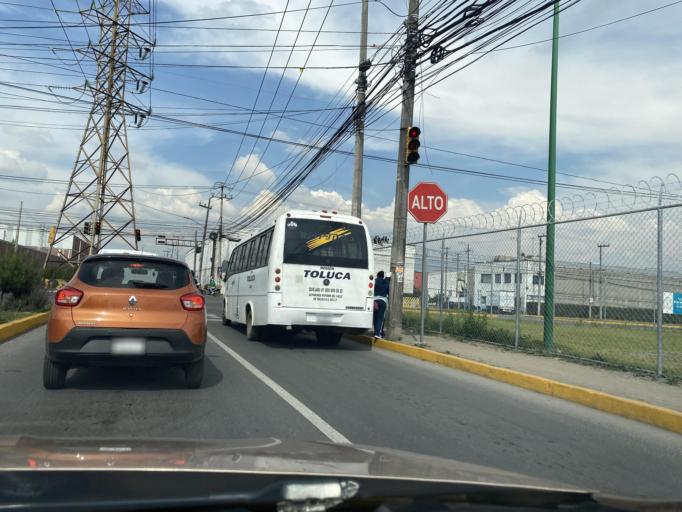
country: IN
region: Karnataka
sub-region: Dakshina Kannada
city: Puttur
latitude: 12.7376
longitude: 75.1834
